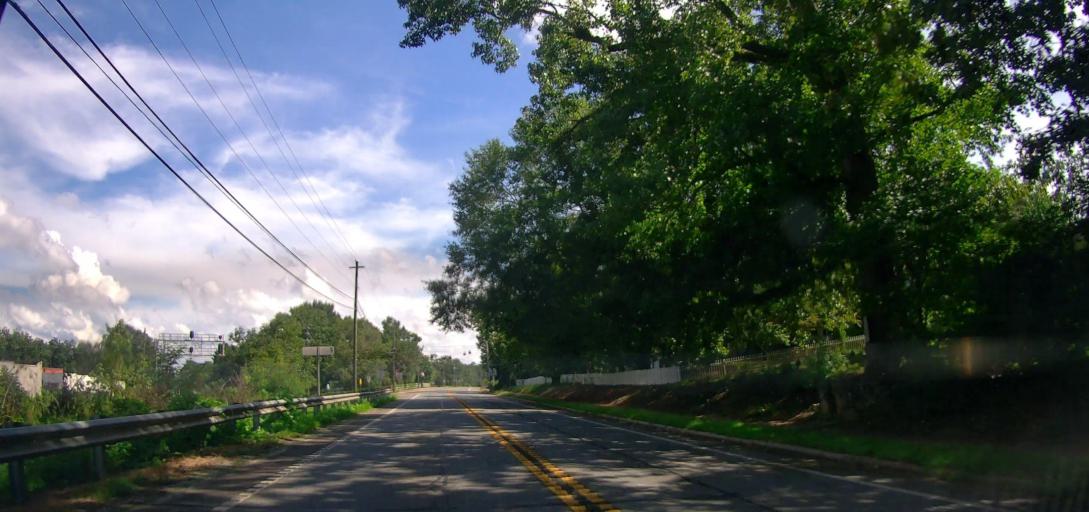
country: US
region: Georgia
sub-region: Talbot County
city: Sardis
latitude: 32.7883
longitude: -84.5623
